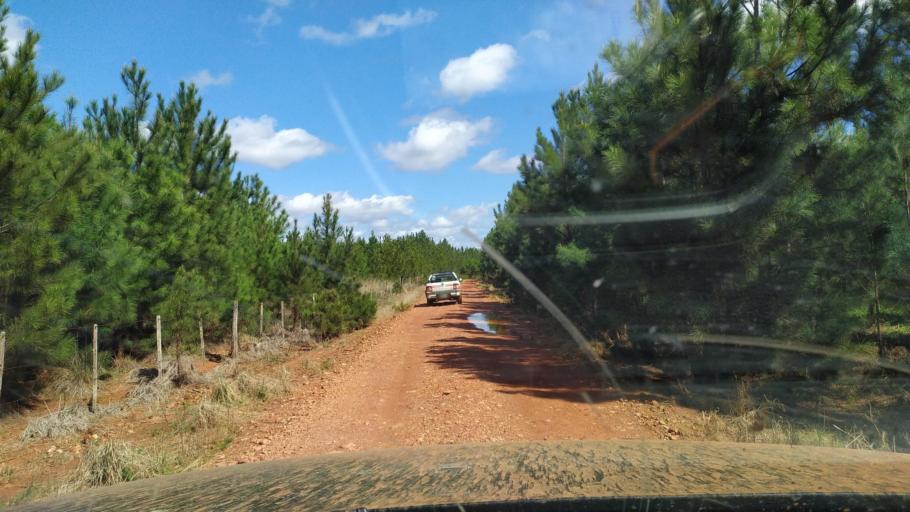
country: AR
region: Corrientes
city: Santo Tome
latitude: -28.4667
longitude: -55.9793
